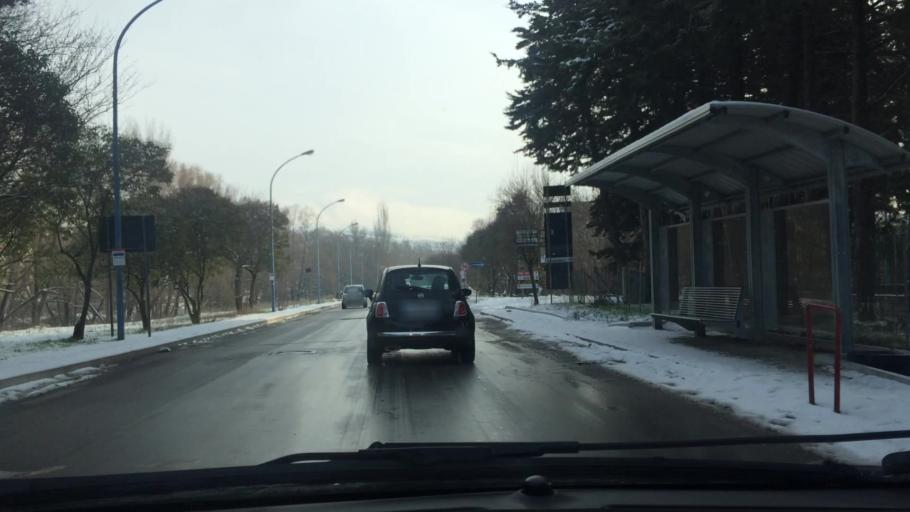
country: IT
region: Basilicate
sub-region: Provincia di Potenza
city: Potenza
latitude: 40.6279
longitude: 15.8080
